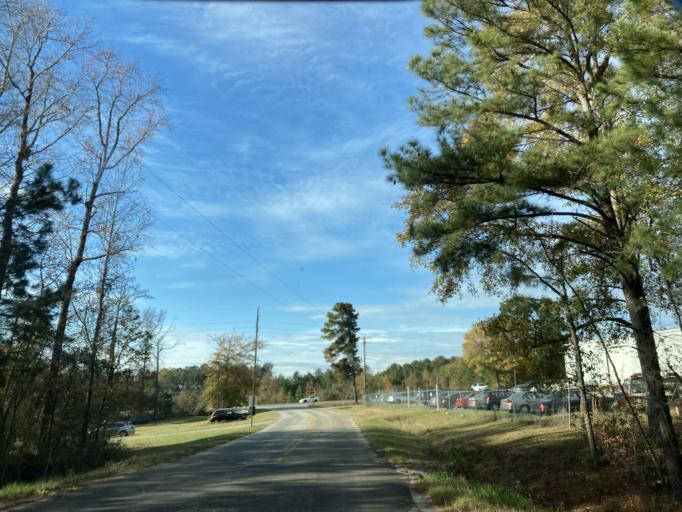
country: US
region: Georgia
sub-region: Jones County
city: Gray
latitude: 32.9150
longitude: -83.5152
